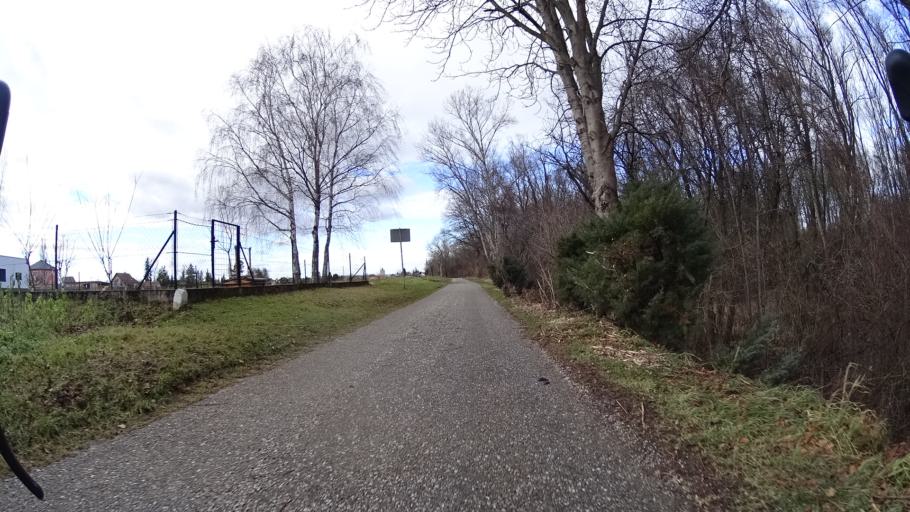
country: AT
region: Lower Austria
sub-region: Politischer Bezirk Tulln
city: Michelhausen
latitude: 48.3410
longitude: 15.9313
